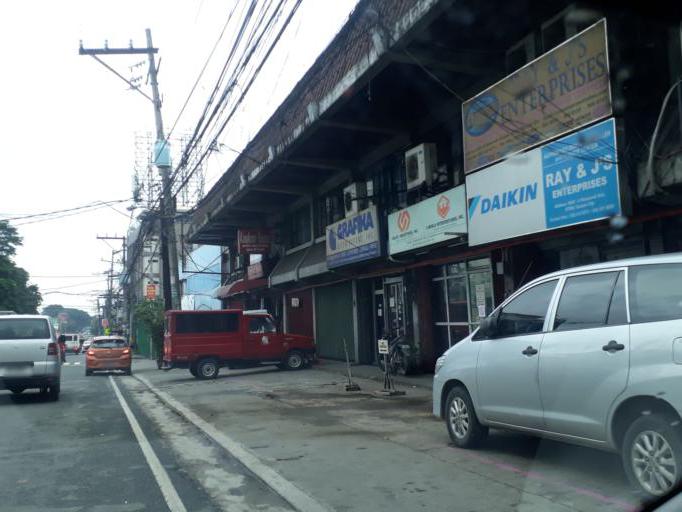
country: PH
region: Calabarzon
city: Del Monte
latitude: 14.6472
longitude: 121.0184
